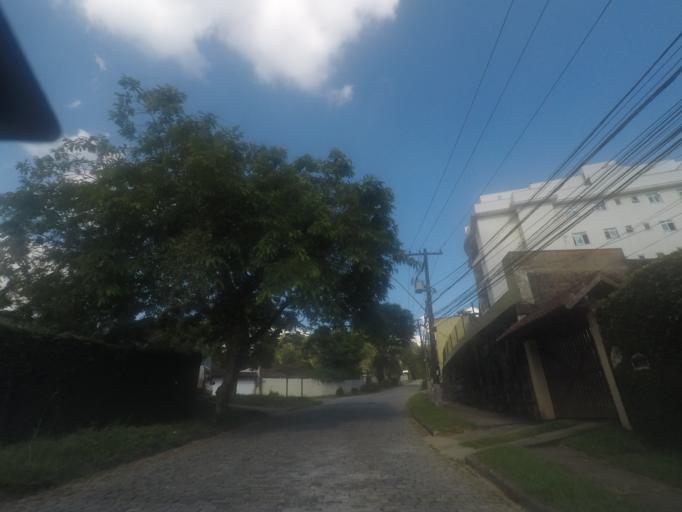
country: BR
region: Rio de Janeiro
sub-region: Petropolis
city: Petropolis
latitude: -22.5214
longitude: -43.2059
